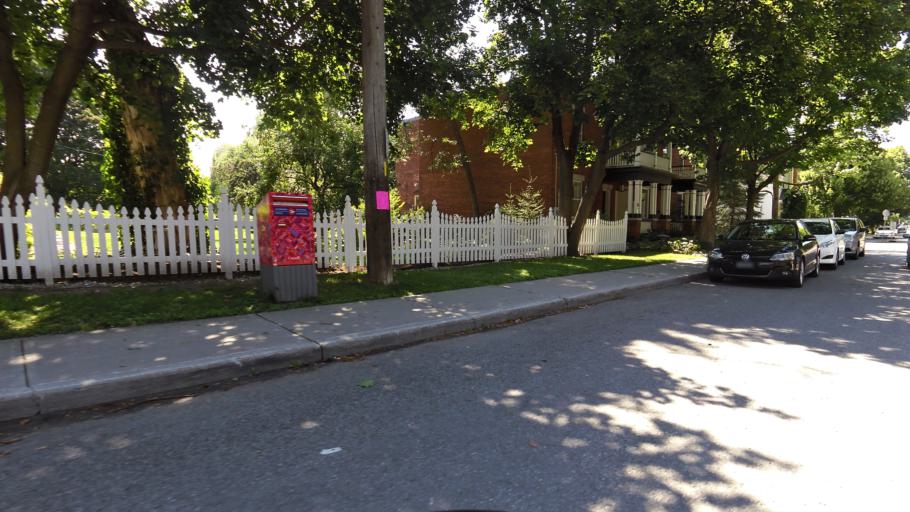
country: CA
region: Ontario
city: Ottawa
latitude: 45.4400
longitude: -75.6882
